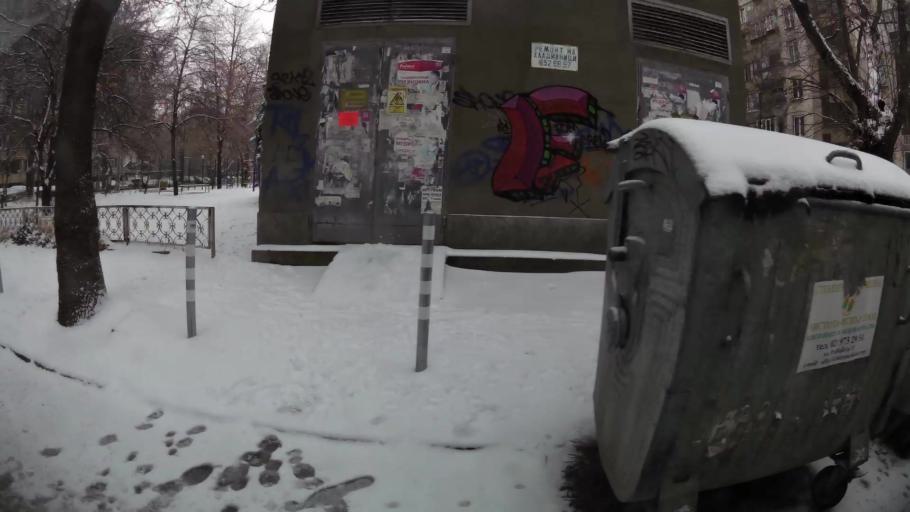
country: BG
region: Sofia-Capital
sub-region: Stolichna Obshtina
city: Sofia
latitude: 42.6875
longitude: 23.3062
